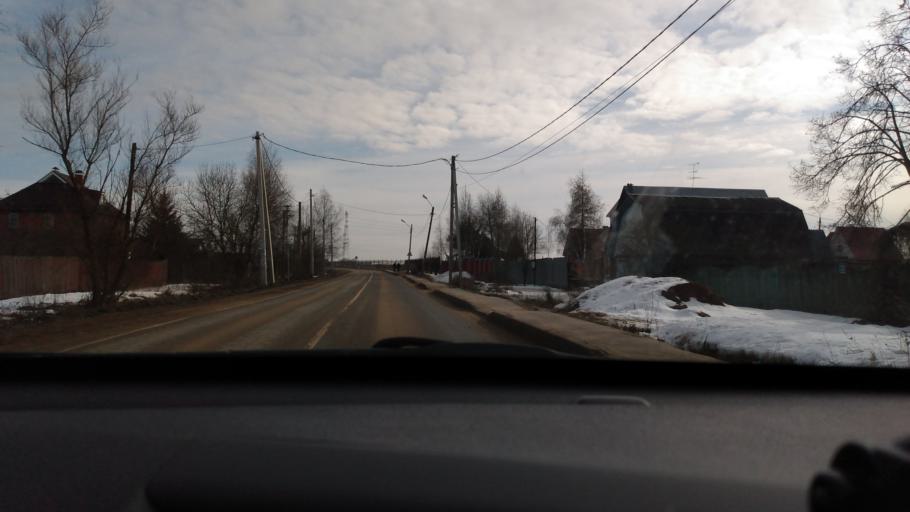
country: RU
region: Moskovskaya
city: Dedovsk
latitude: 55.8930
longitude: 37.1595
